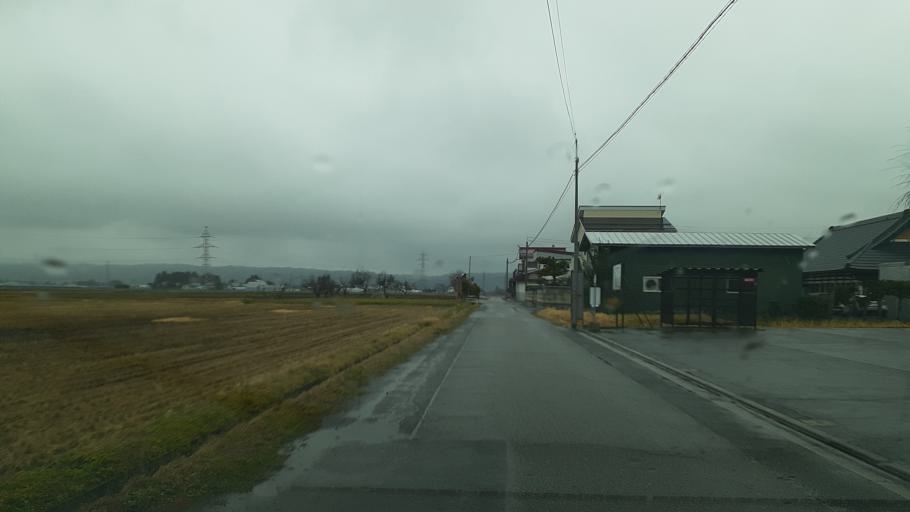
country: JP
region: Fukushima
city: Kitakata
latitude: 37.5834
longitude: 139.8464
